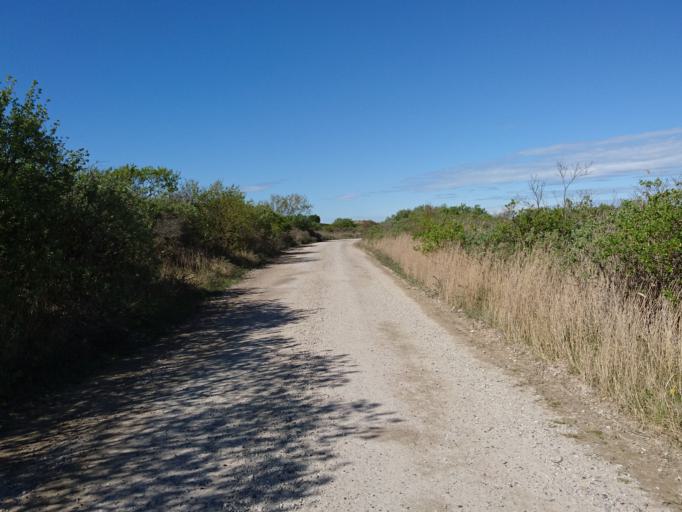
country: DK
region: North Denmark
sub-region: Frederikshavn Kommune
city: Skagen
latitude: 57.7432
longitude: 10.6345
